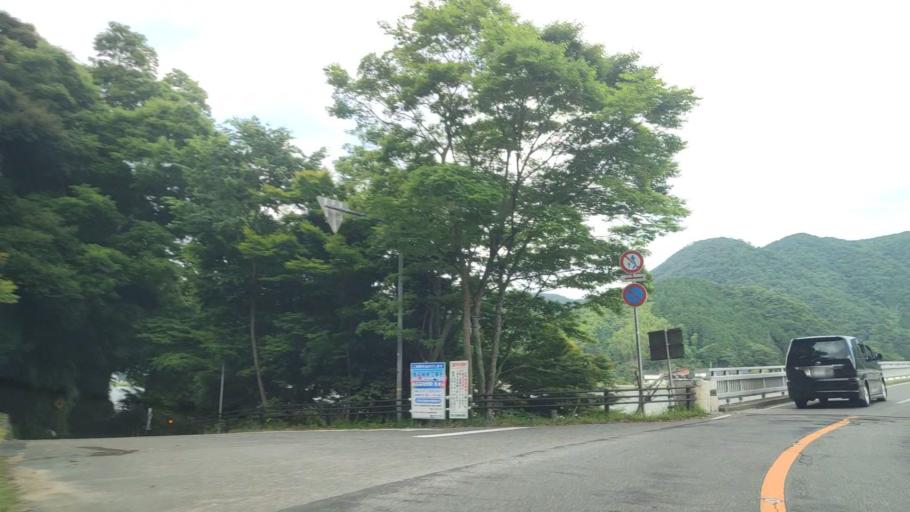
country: JP
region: Hyogo
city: Toyooka
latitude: 35.6408
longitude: 134.8283
